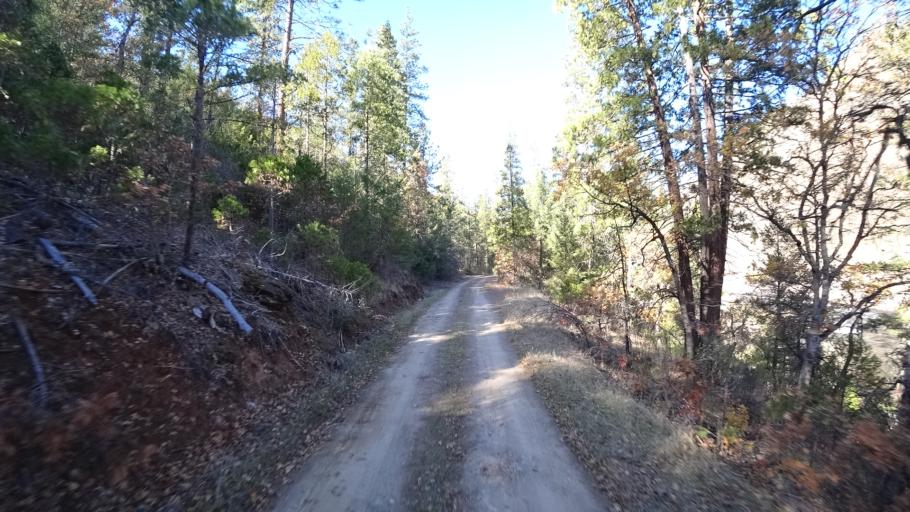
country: US
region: California
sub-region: Siskiyou County
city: Yreka
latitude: 41.8539
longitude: -122.7691
